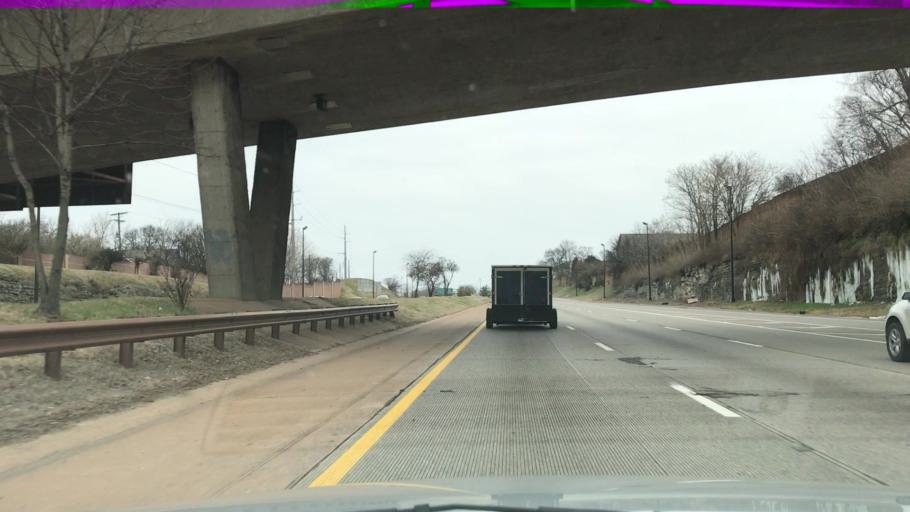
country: US
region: Tennessee
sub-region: Davidson County
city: Nashville
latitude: 36.1428
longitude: -86.8226
